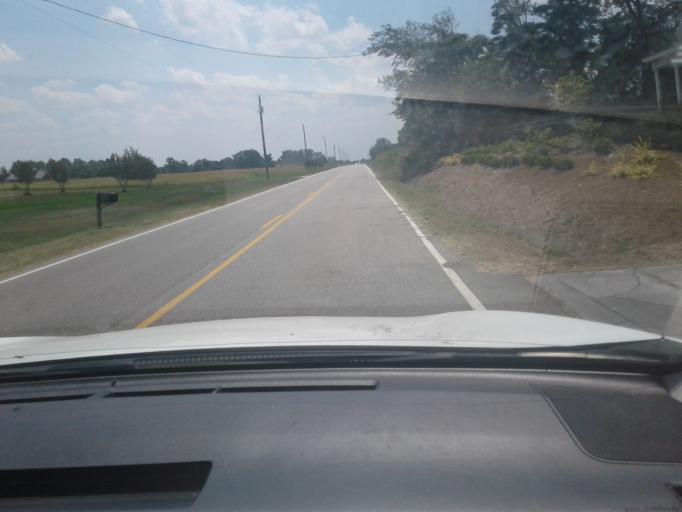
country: US
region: North Carolina
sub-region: Harnett County
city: Coats
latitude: 35.3787
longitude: -78.6221
